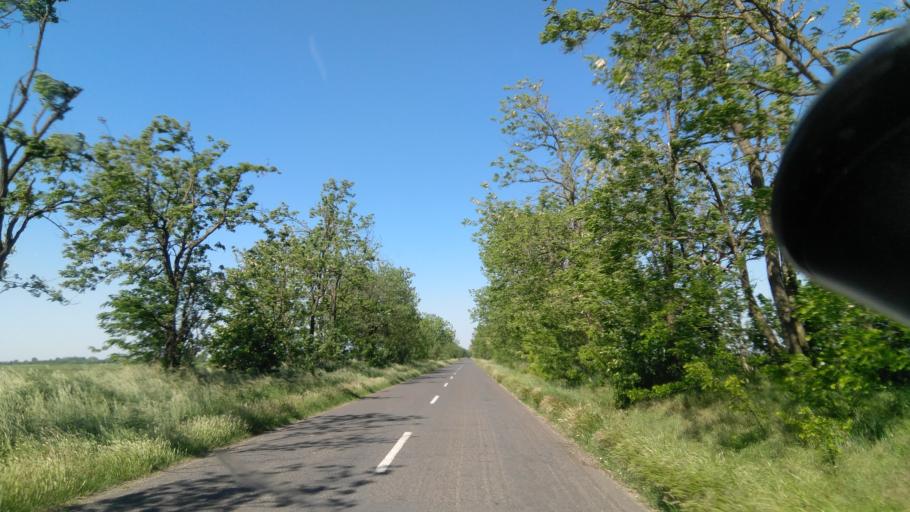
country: HU
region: Bekes
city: Kevermes
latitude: 46.4256
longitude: 21.1478
